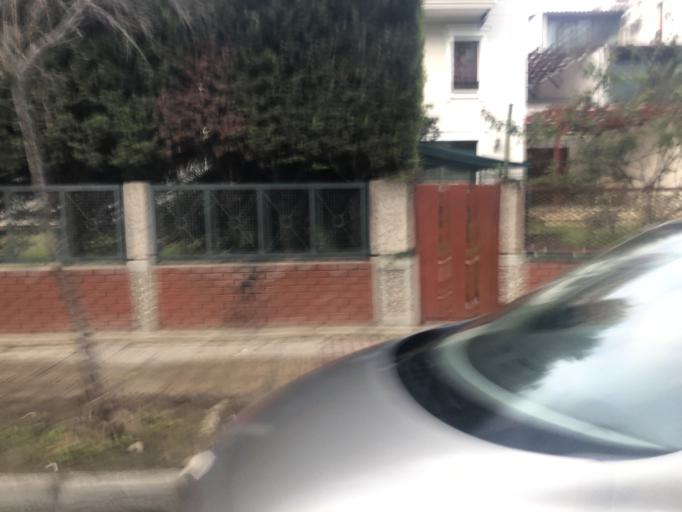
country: TR
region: Izmir
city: Karsiyaka
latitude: 38.4694
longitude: 27.0723
